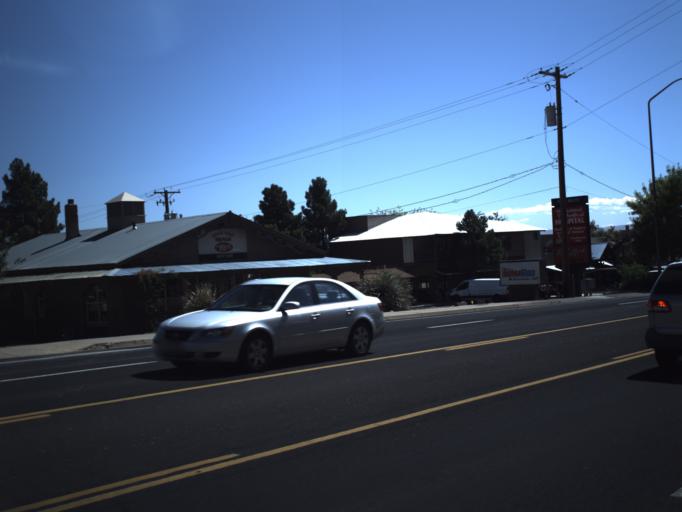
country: US
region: Utah
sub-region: Washington County
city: Saint George
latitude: 37.1078
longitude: -113.5932
